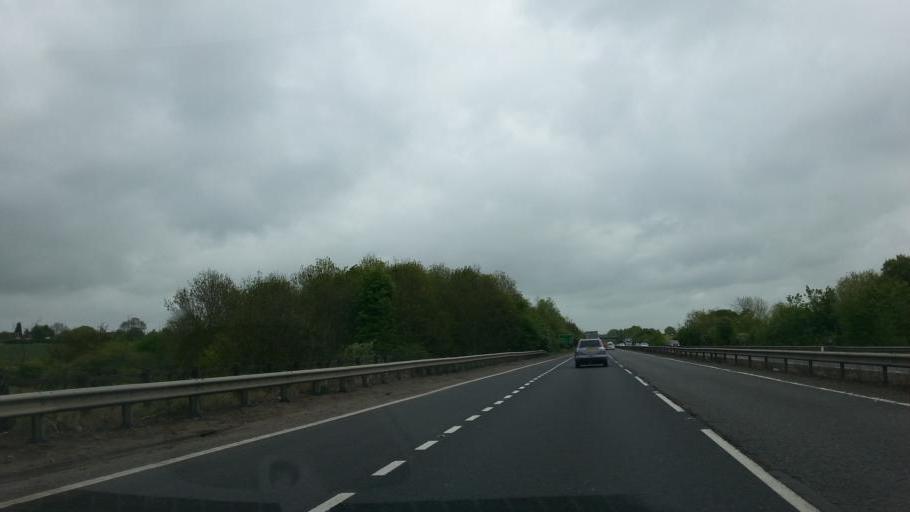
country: GB
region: England
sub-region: Suffolk
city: Stowmarket
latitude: 52.1838
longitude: 1.0308
